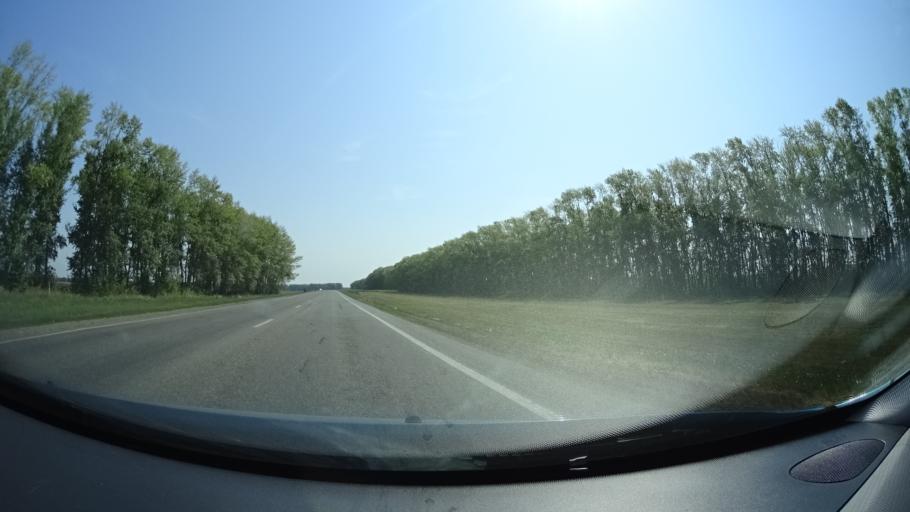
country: RU
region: Bashkortostan
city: Karmaskaly
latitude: 54.3907
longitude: 56.1230
